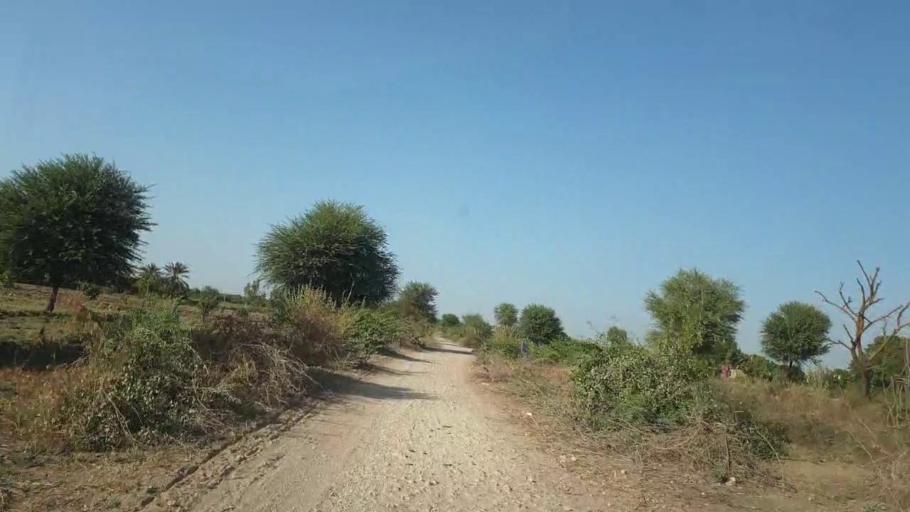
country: PK
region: Sindh
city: Kunri
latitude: 25.0599
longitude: 69.4420
